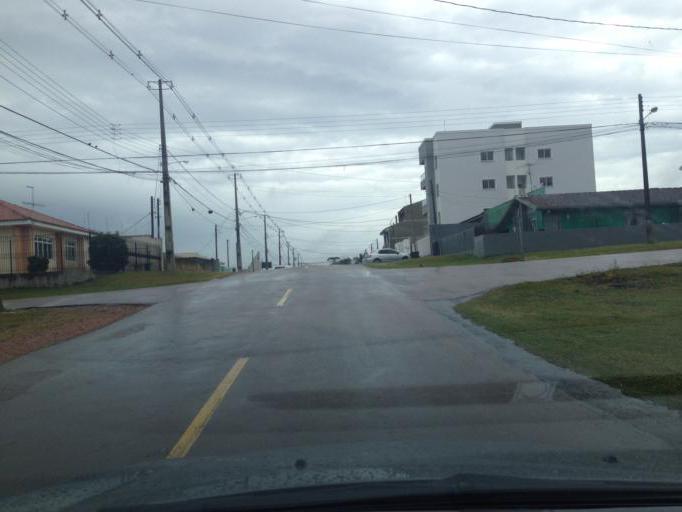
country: BR
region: Parana
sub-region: Sao Jose Dos Pinhais
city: Sao Jose dos Pinhais
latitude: -25.5418
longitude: -49.1826
